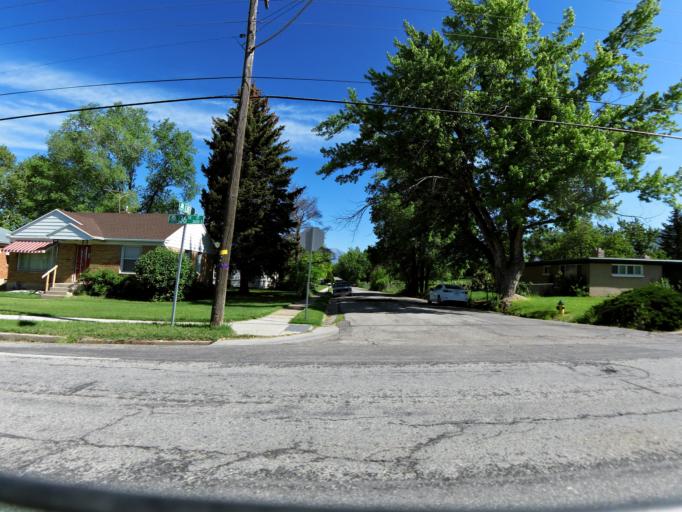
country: US
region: Utah
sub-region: Weber County
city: South Ogden
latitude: 41.1976
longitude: -111.9618
